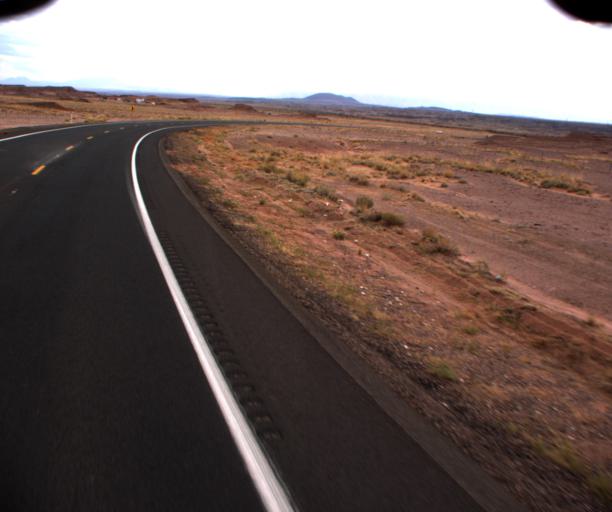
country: US
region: Arizona
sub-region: Coconino County
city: Tuba City
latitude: 36.0841
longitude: -111.3678
